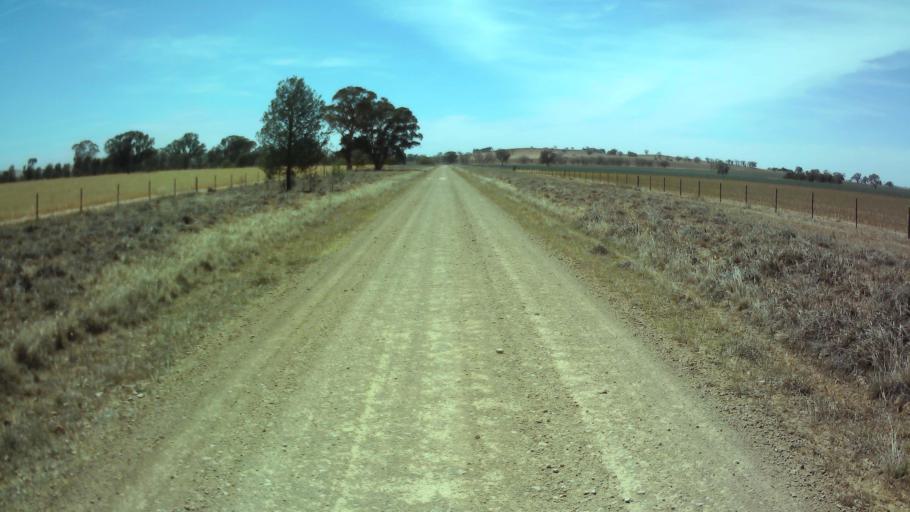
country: AU
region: New South Wales
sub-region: Weddin
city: Grenfell
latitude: -33.9918
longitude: 148.1479
